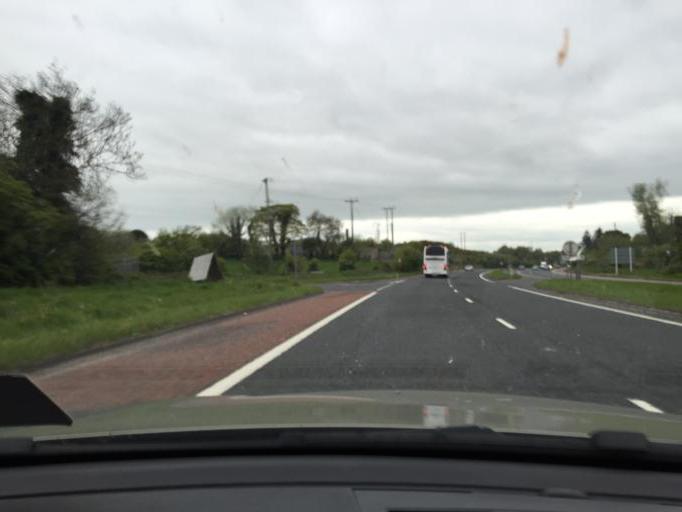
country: GB
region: Northern Ireland
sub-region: Banbridge District
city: Banbridge
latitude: 54.3612
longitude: -6.2275
